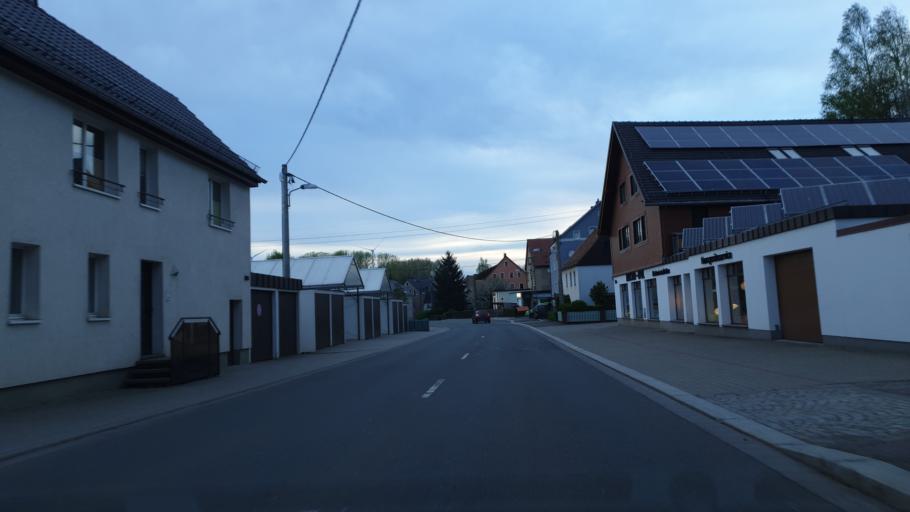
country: DE
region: Saxony
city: Gersdorf
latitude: 50.7519
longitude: 12.7097
